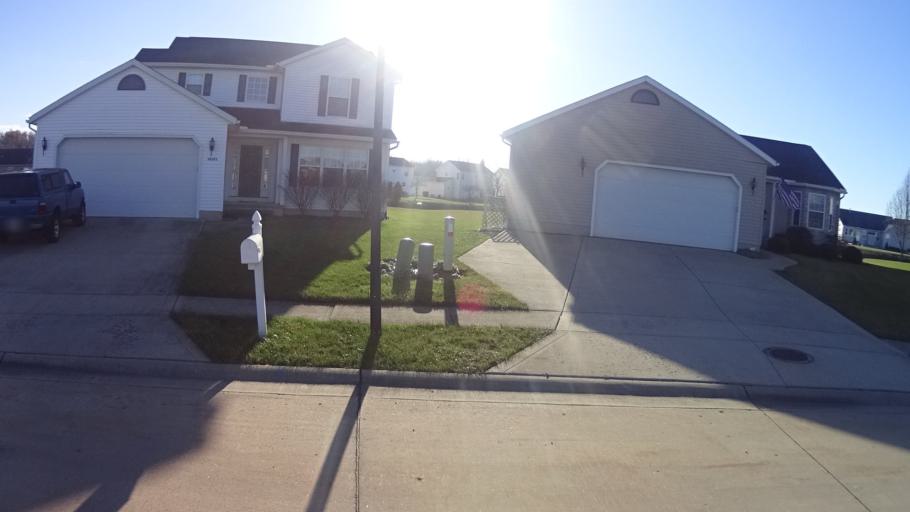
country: US
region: Ohio
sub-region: Lorain County
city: North Ridgeville
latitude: 41.4100
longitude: -82.0535
